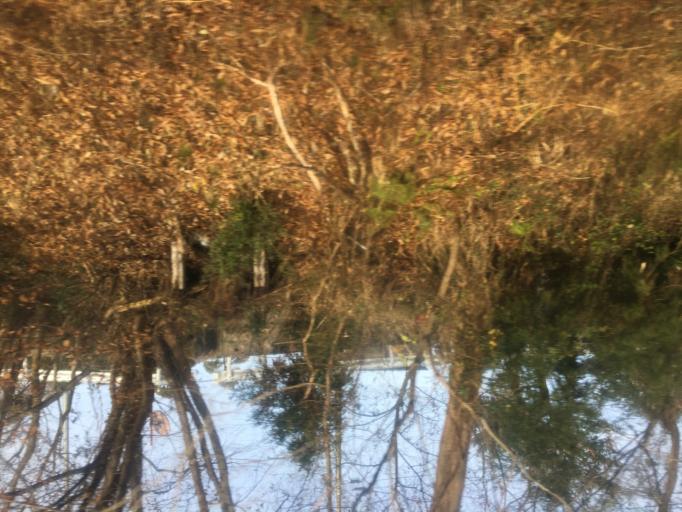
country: JP
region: Akita
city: Odate
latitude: 40.2711
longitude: 140.4563
